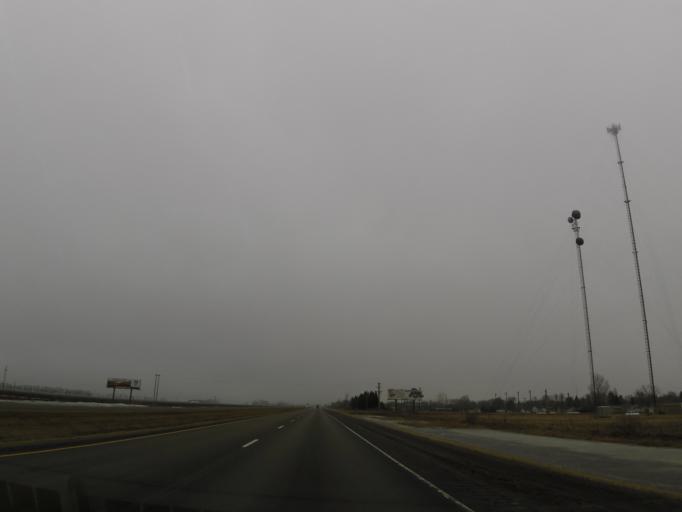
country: US
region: North Dakota
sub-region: Walsh County
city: Grafton
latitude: 48.5547
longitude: -97.1860
